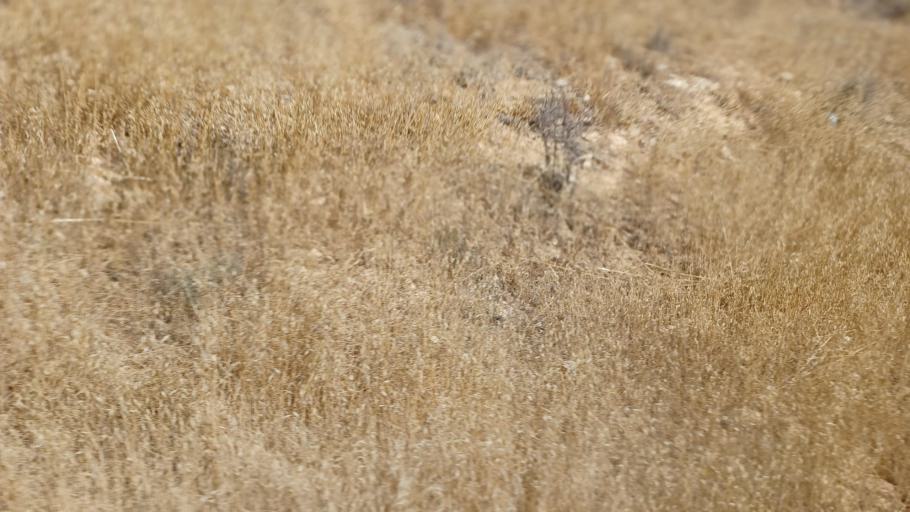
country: CY
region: Ammochostos
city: Liopetri
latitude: 34.9830
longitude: 33.8791
